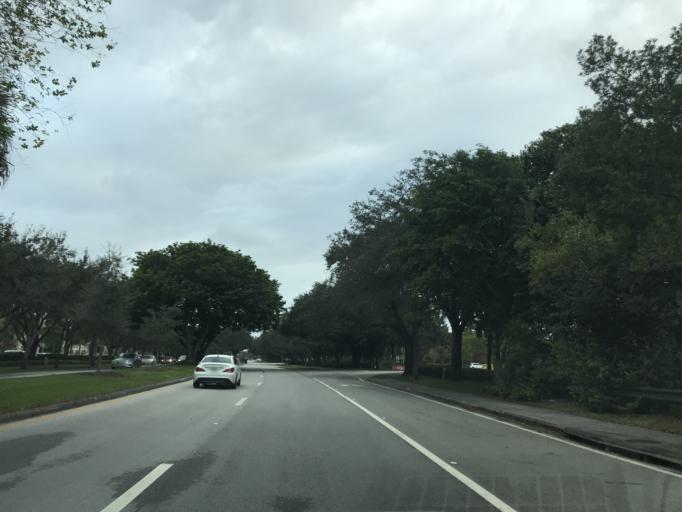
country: US
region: Florida
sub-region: Broward County
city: Parkland
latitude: 26.2990
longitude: -80.2464
